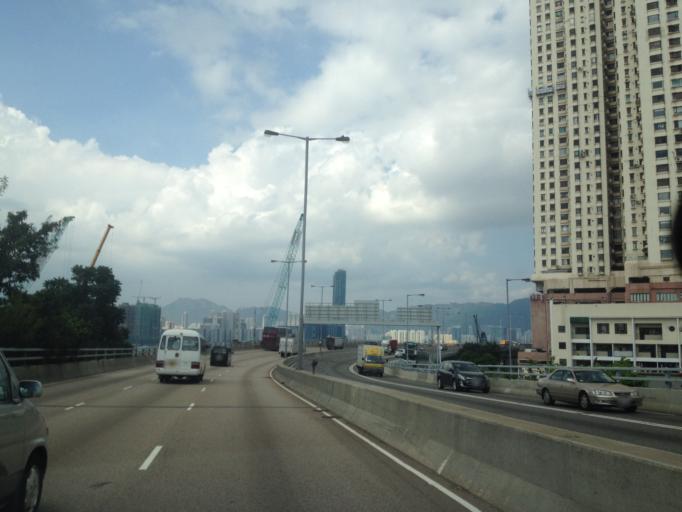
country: HK
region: Wanchai
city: Wan Chai
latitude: 22.2861
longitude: 114.1893
